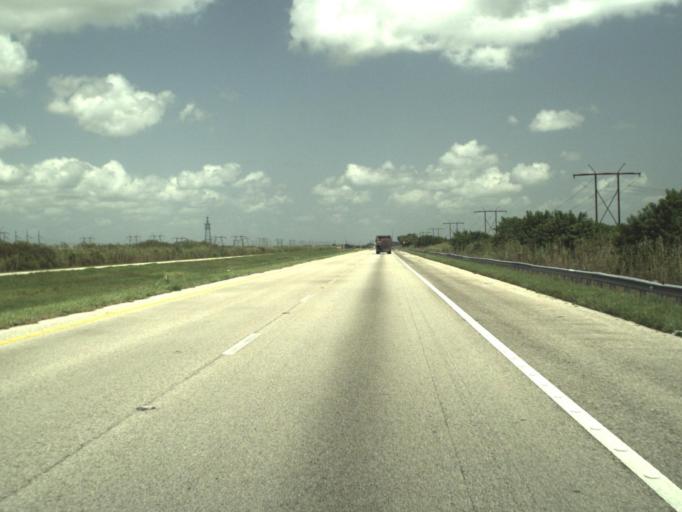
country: US
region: Florida
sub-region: Broward County
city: Weston
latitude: 26.2949
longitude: -80.5068
